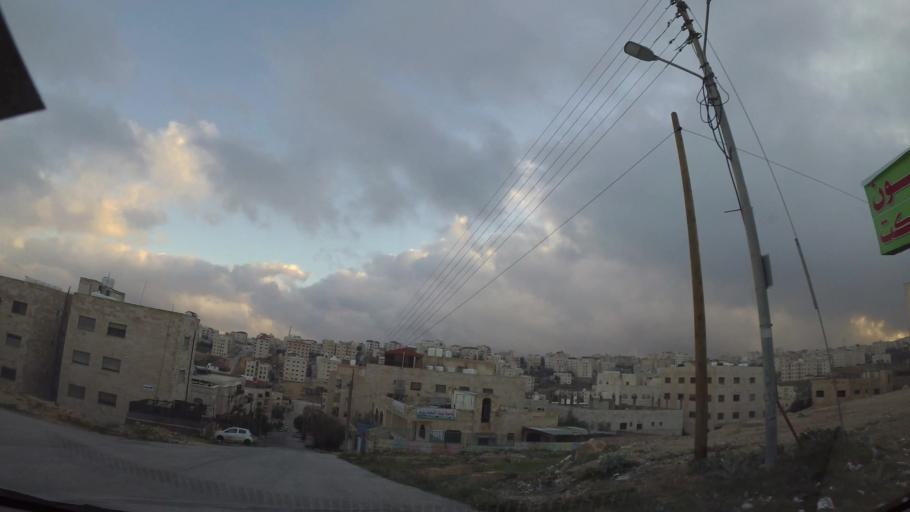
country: JO
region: Amman
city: Al Jubayhah
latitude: 32.0538
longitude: 35.8941
